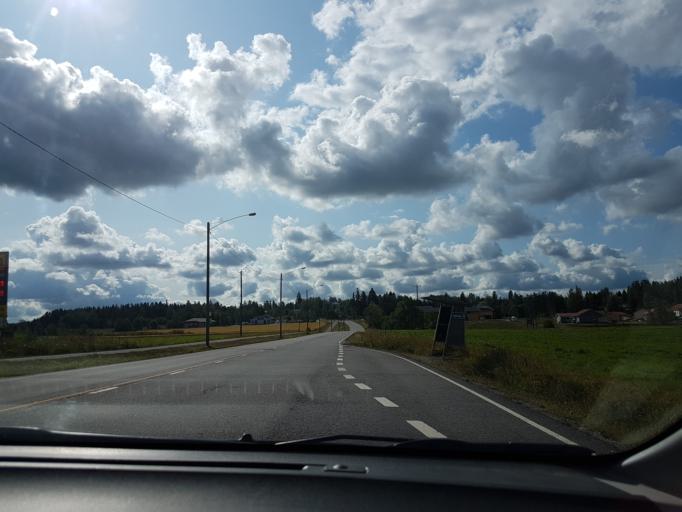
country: FI
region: Uusimaa
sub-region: Helsinki
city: Pornainen
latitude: 60.4837
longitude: 25.3689
